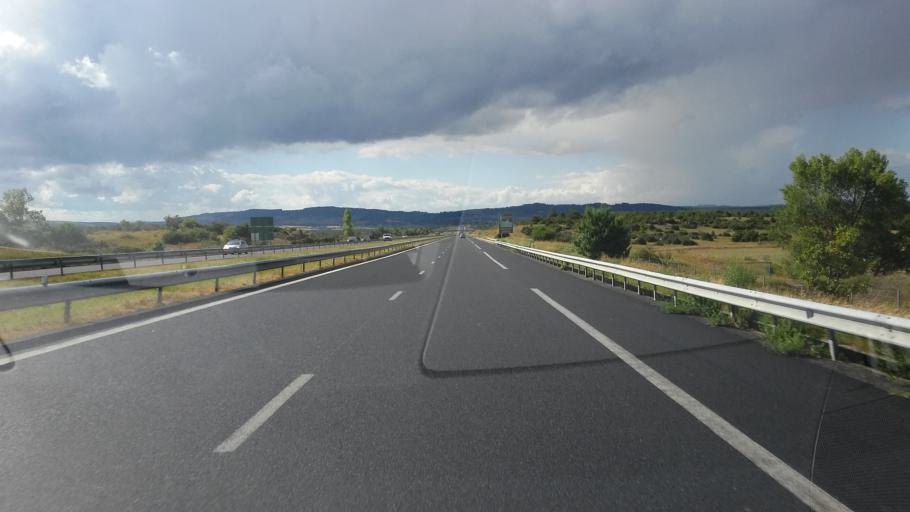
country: FR
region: Midi-Pyrenees
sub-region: Departement de l'Aveyron
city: La Cavalerie
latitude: 43.9263
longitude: 3.2381
